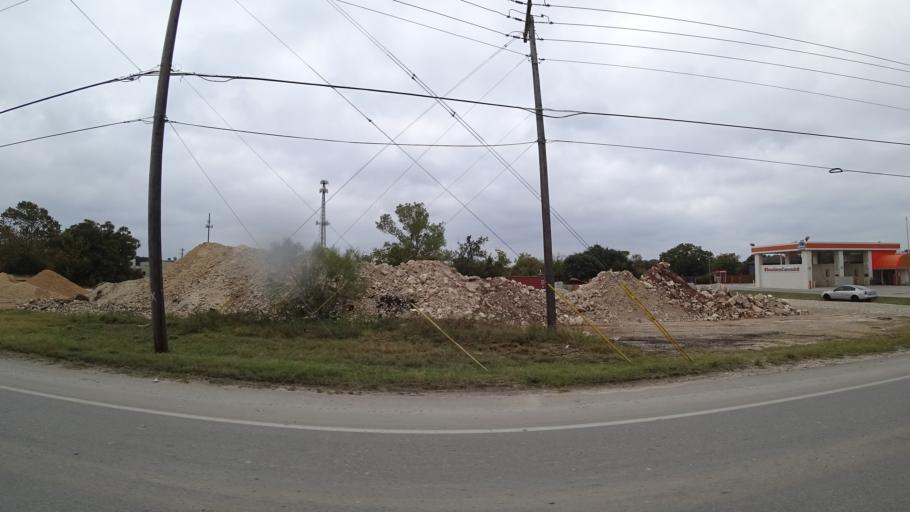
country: US
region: Texas
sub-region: Williamson County
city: Cedar Park
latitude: 30.5154
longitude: -97.8480
